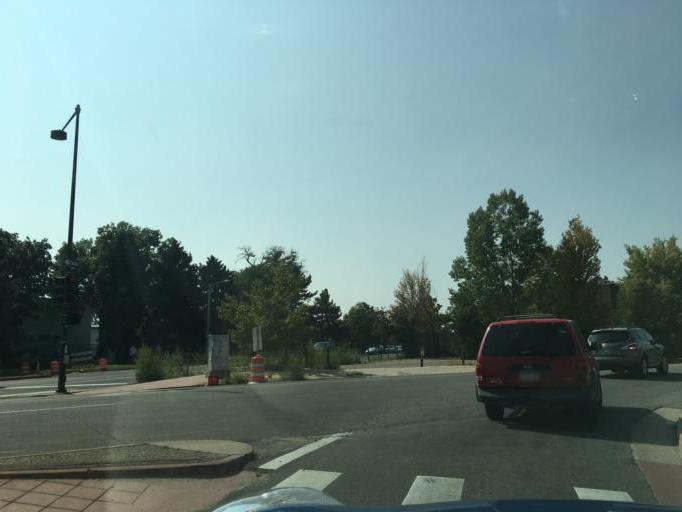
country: US
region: Colorado
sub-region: Denver County
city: Denver
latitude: 39.7703
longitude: -104.9723
